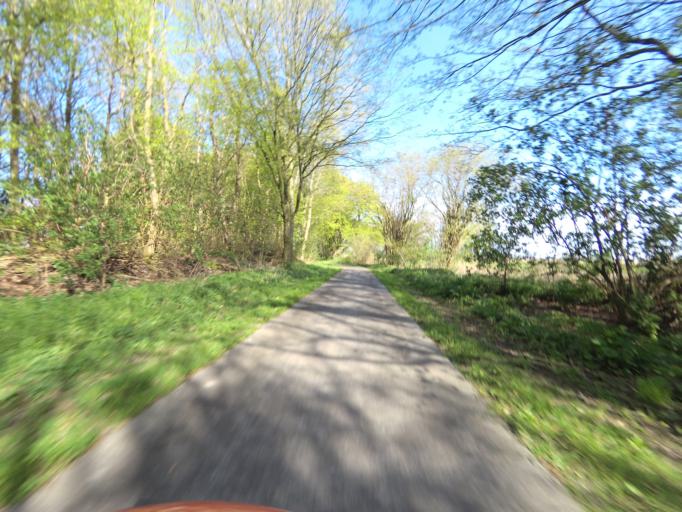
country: NL
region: Gelderland
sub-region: Gemeente Harderwijk
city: Harderwijk
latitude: 52.4224
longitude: 5.5792
